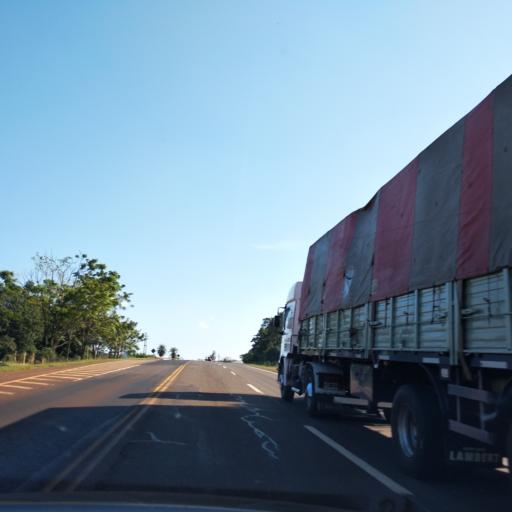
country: AR
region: Misiones
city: Jardin America
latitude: -27.0972
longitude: -55.3025
